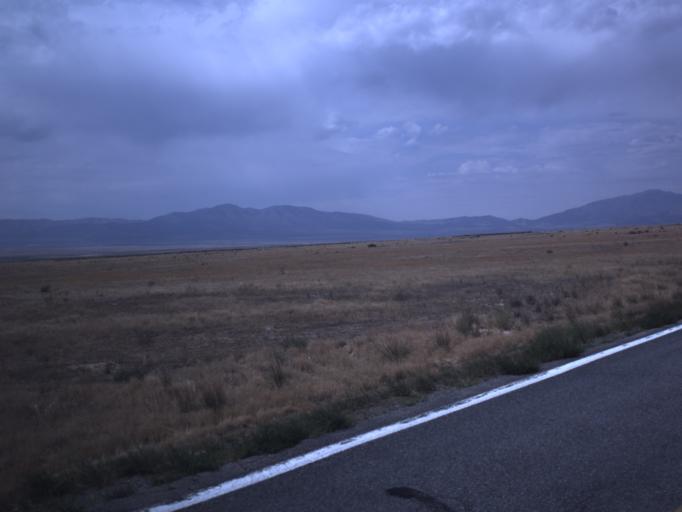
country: US
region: Utah
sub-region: Utah County
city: Eagle Mountain
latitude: 40.2443
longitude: -112.2098
